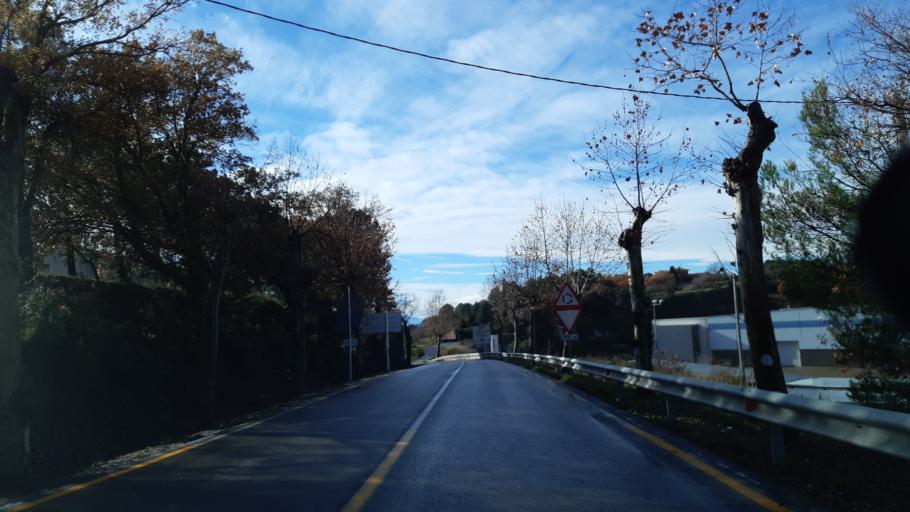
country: ES
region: Catalonia
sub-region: Provincia de Tarragona
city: Falset
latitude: 41.1429
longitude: 0.8125
